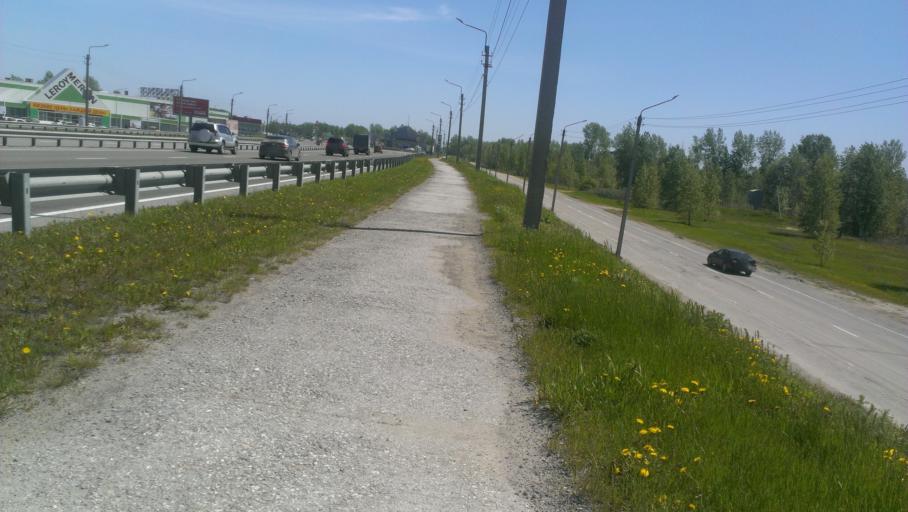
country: RU
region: Altai Krai
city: Zaton
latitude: 53.3160
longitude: 83.8254
